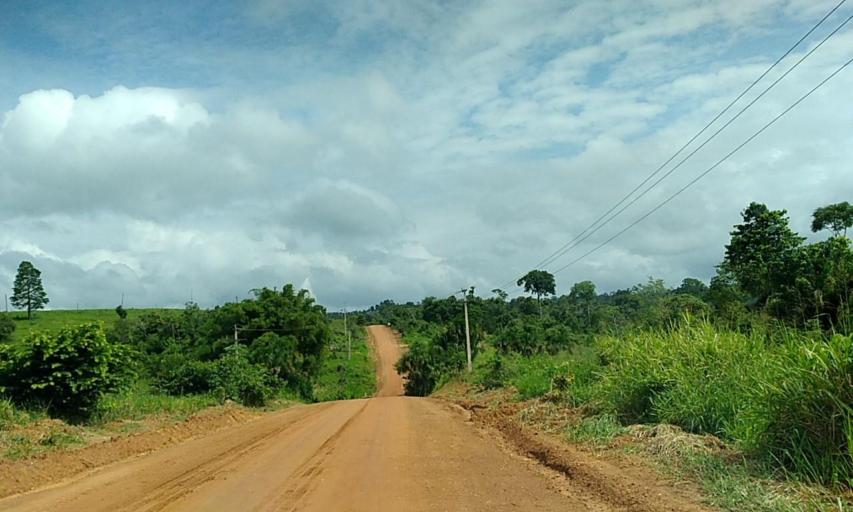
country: BR
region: Para
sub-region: Senador Jose Porfirio
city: Senador Jose Porfirio
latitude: -3.0614
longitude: -51.6352
